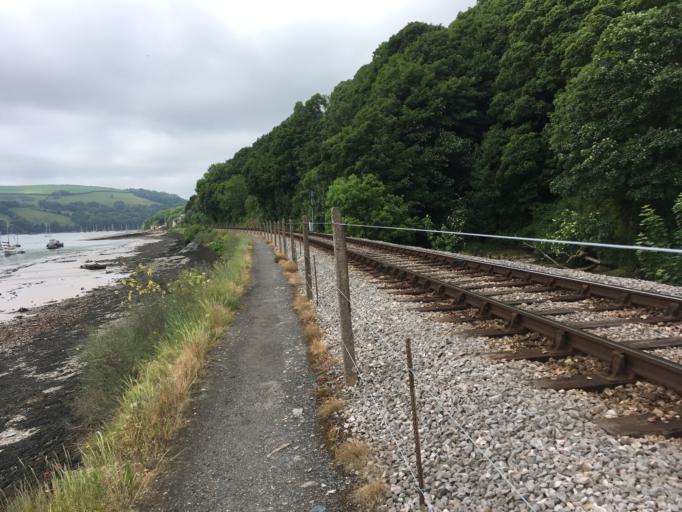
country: GB
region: England
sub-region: Devon
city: Dartmouth
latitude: 50.3568
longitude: -3.5704
